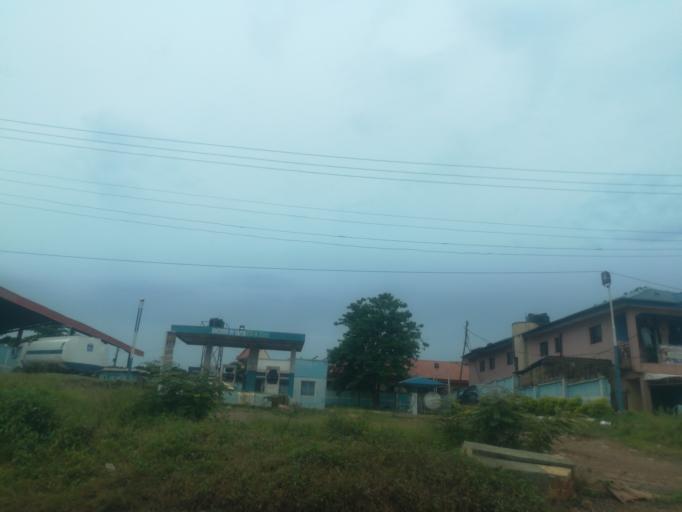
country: NG
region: Oyo
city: Ibadan
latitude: 7.3919
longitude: 3.9619
